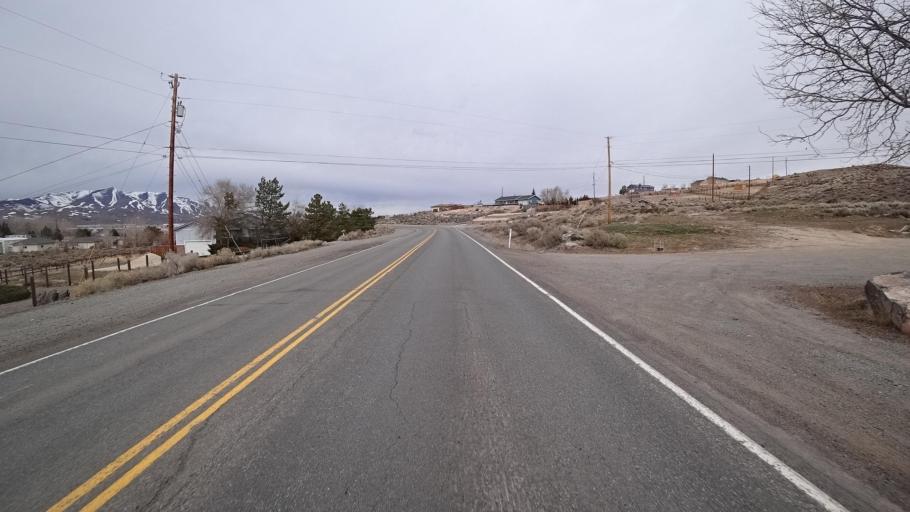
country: US
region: Nevada
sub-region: Washoe County
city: Golden Valley
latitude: 39.6072
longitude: -119.8124
